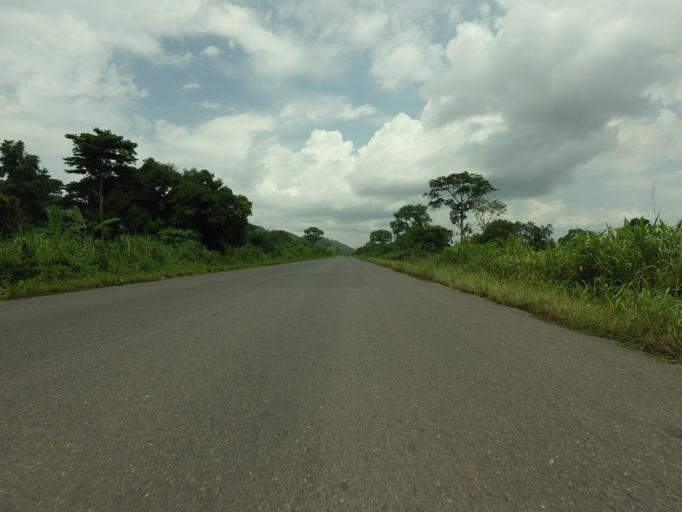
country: GH
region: Volta
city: Ho
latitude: 6.4904
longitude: 0.2004
